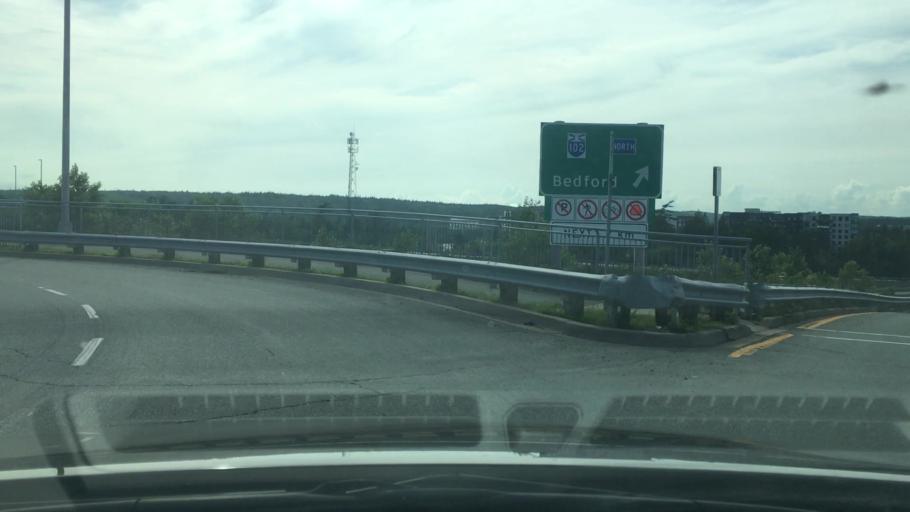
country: CA
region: Nova Scotia
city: Dartmouth
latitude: 44.6994
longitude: -63.6900
